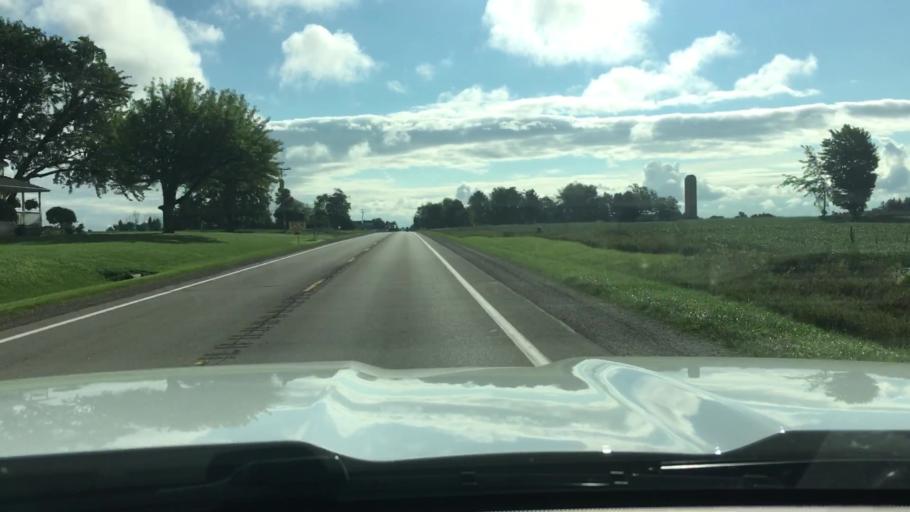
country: US
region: Michigan
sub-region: Tuscola County
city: Cass City
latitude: 43.5999
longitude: -83.2209
